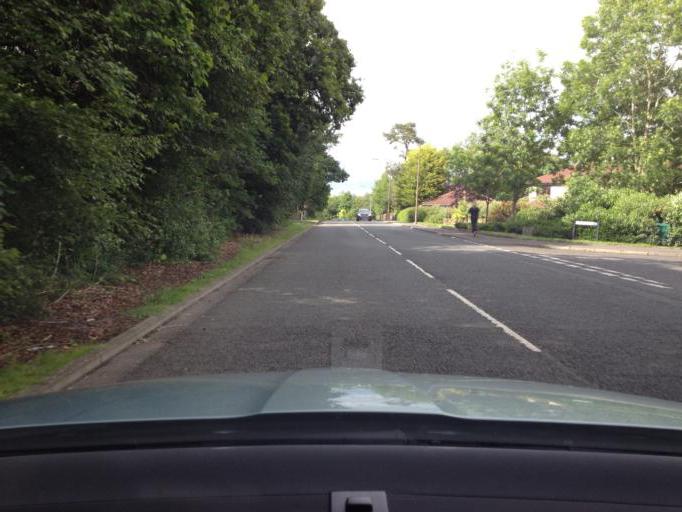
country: GB
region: Scotland
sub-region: West Lothian
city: Livingston
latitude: 55.8614
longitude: -3.5192
